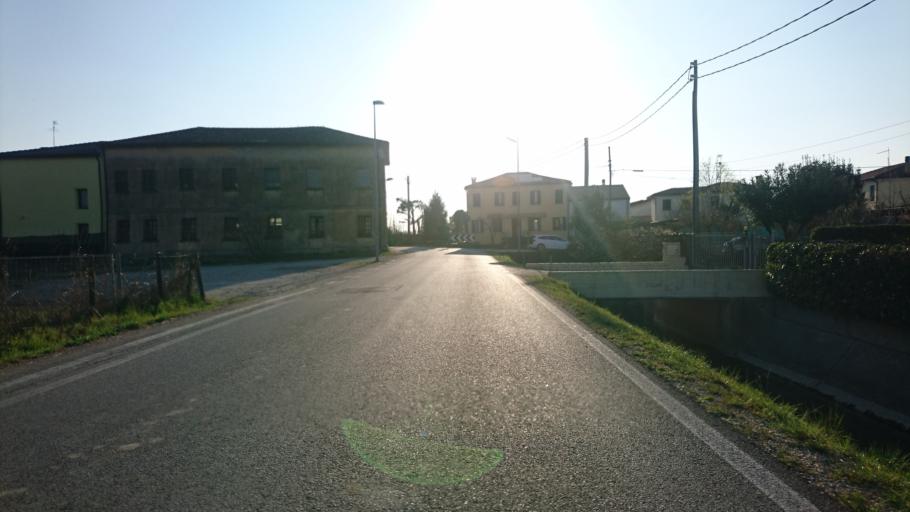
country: IT
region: Veneto
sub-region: Provincia di Padova
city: Vigonza
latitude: 45.4379
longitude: 11.9857
